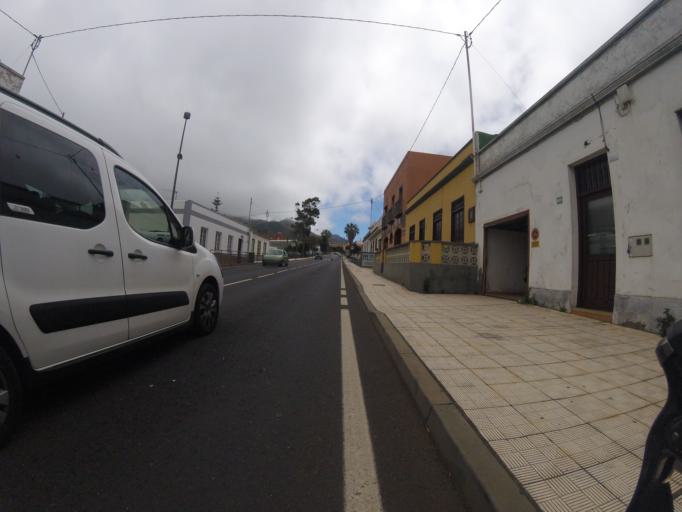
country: ES
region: Canary Islands
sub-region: Provincia de Santa Cruz de Tenerife
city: Tegueste
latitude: 28.5225
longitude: -16.3423
